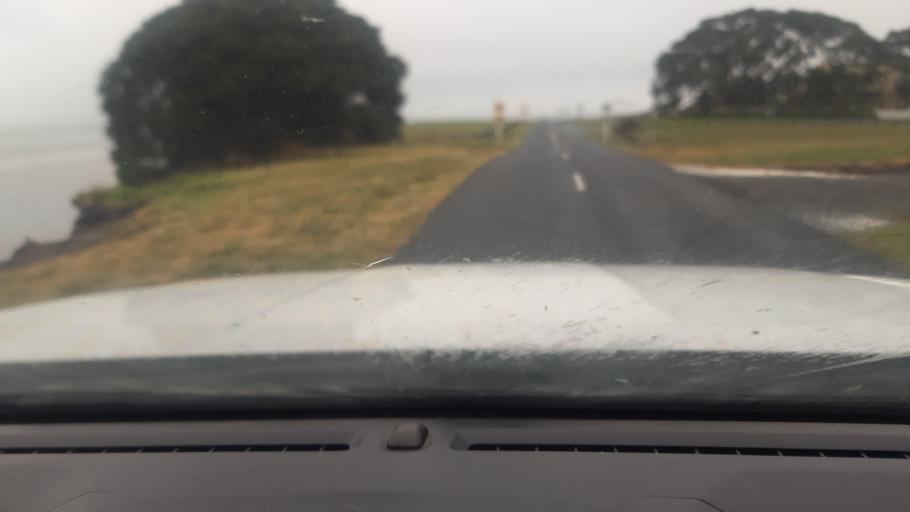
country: NZ
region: Northland
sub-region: Far North District
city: Kaitaia
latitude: -34.9196
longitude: 173.2677
